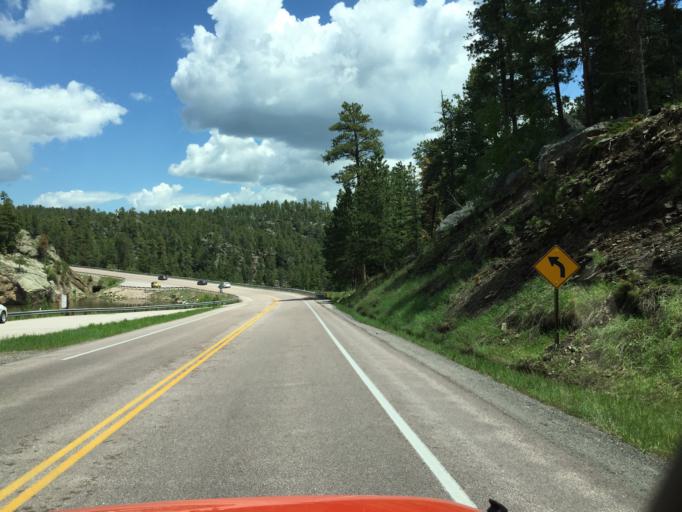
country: US
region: South Dakota
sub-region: Custer County
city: Custer
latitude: 43.8928
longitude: -103.4803
